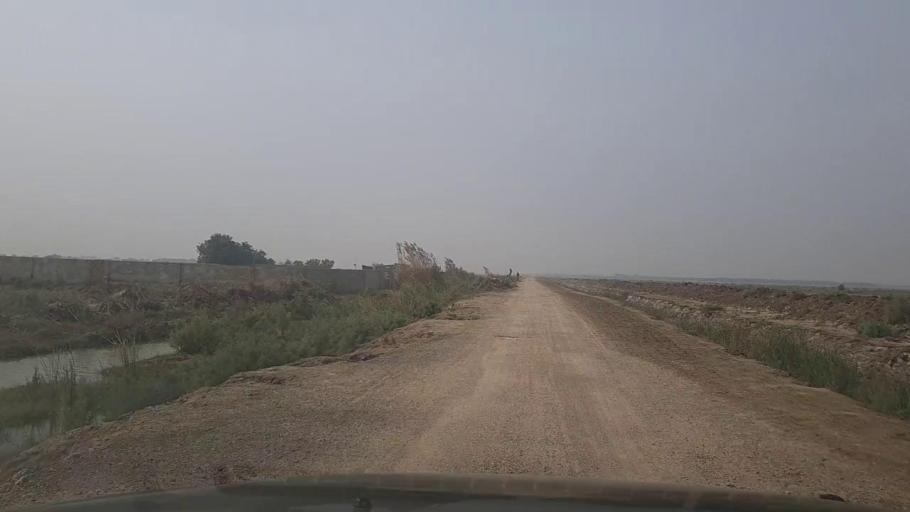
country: PK
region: Sindh
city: Mirpur Sakro
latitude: 24.5320
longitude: 67.7853
